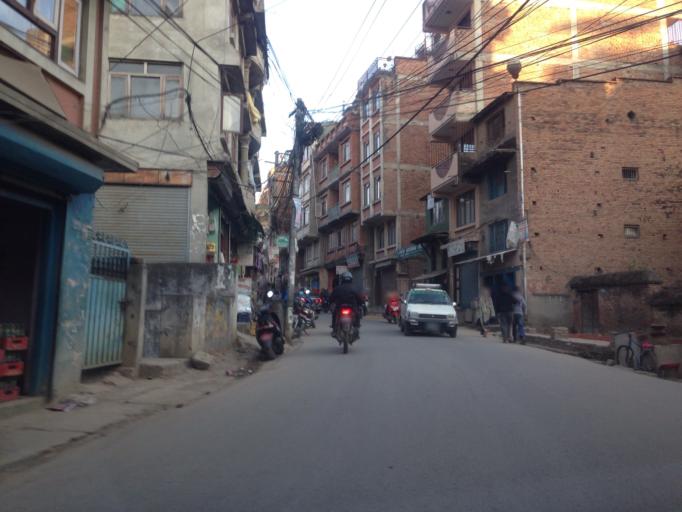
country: NP
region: Central Region
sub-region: Bagmati Zone
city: Kathmandu
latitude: 27.7117
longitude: 85.3062
